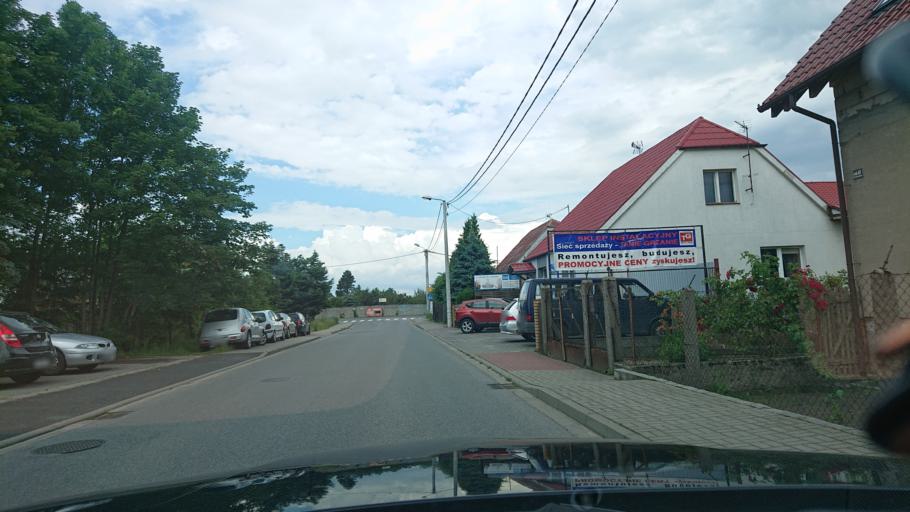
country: PL
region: Greater Poland Voivodeship
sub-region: Powiat gnieznienski
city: Gniezno
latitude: 52.5407
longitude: 17.6341
